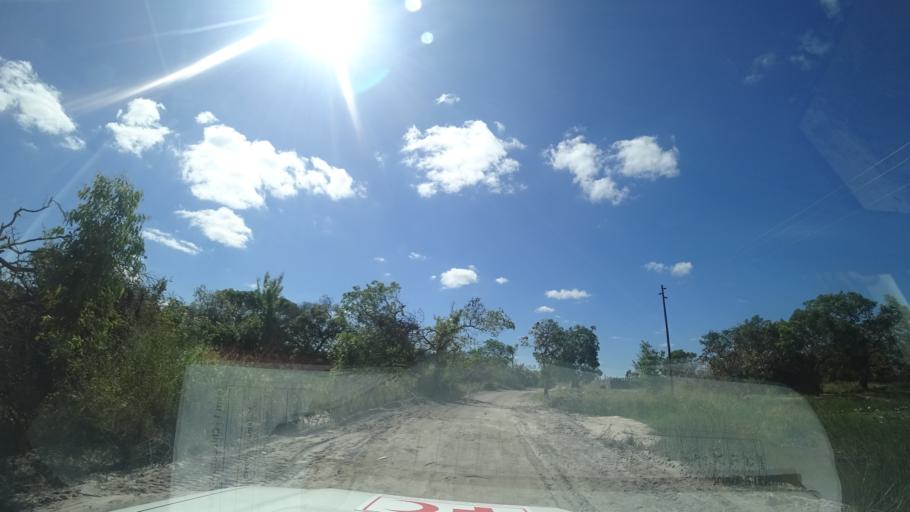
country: MZ
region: Sofala
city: Dondo
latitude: -19.5037
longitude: 34.6119
